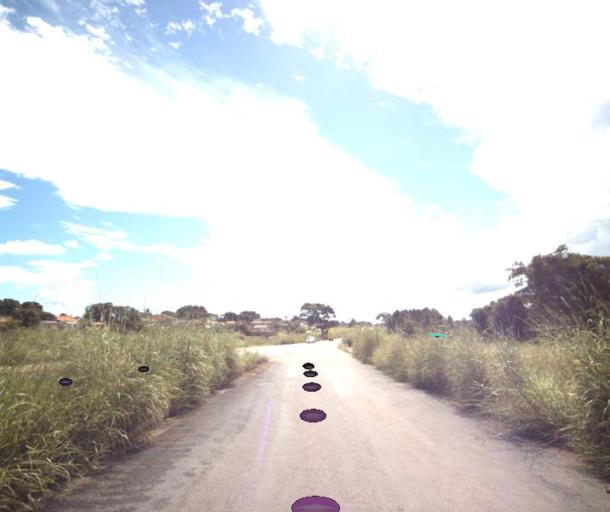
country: BR
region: Goias
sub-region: Pirenopolis
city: Pirenopolis
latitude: -16.0194
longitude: -49.1097
